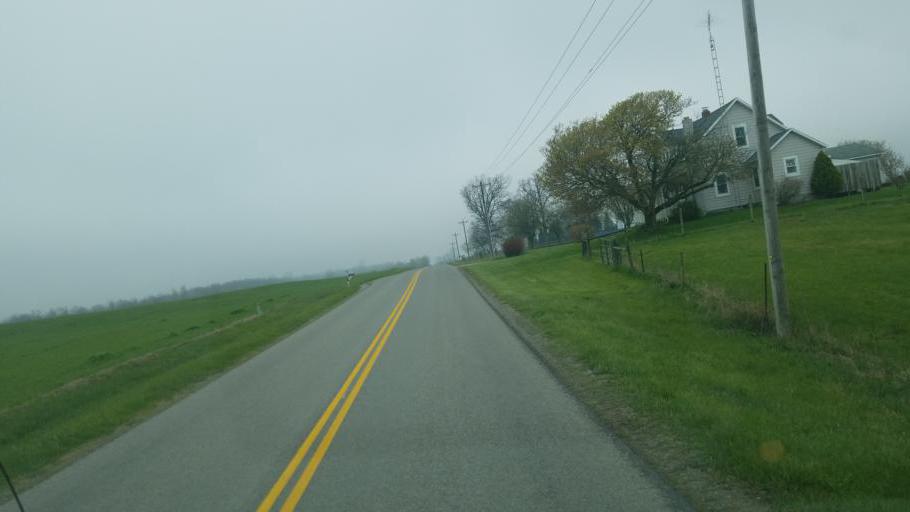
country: US
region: Ohio
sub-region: Logan County
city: Bellefontaine
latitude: 40.3871
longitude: -83.8204
